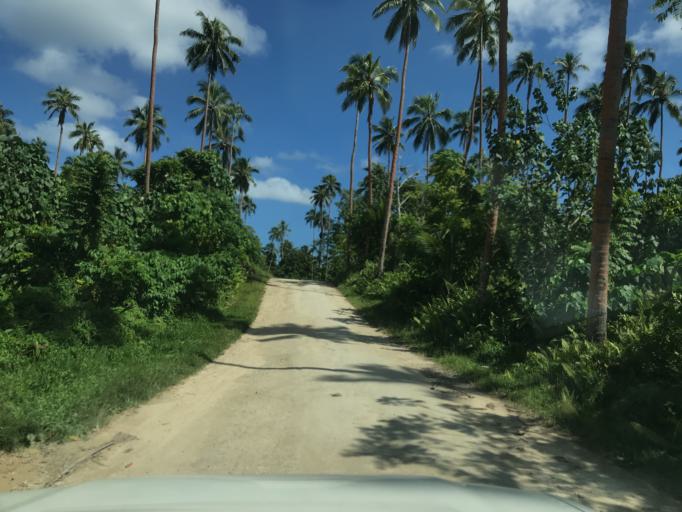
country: VU
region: Sanma
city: Luganville
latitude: -15.5775
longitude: 167.0400
